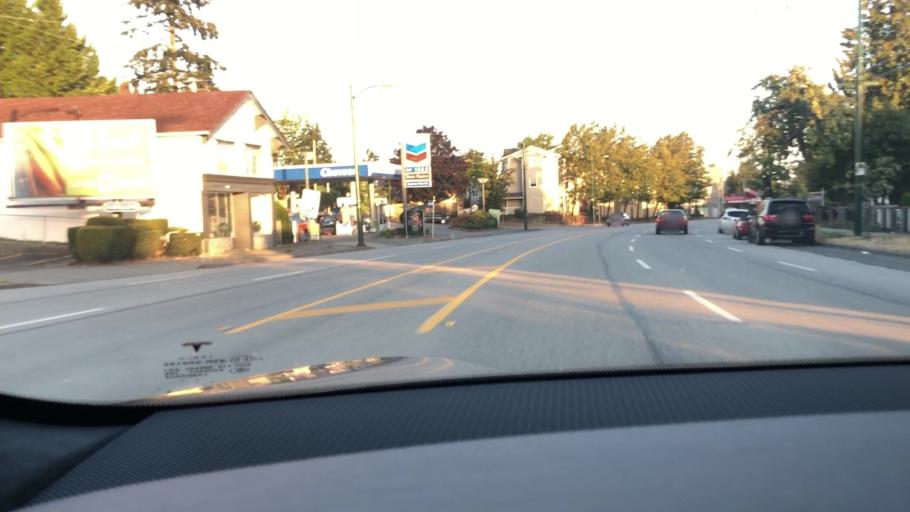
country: CA
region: British Columbia
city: Vancouver
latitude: 49.2362
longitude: -123.0446
